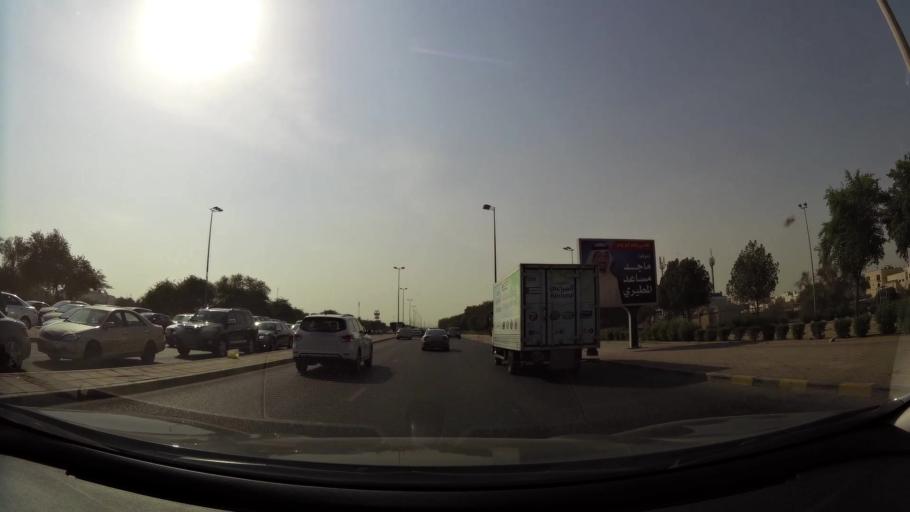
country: KW
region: Al Ahmadi
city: Ar Riqqah
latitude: 29.1580
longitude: 48.0932
